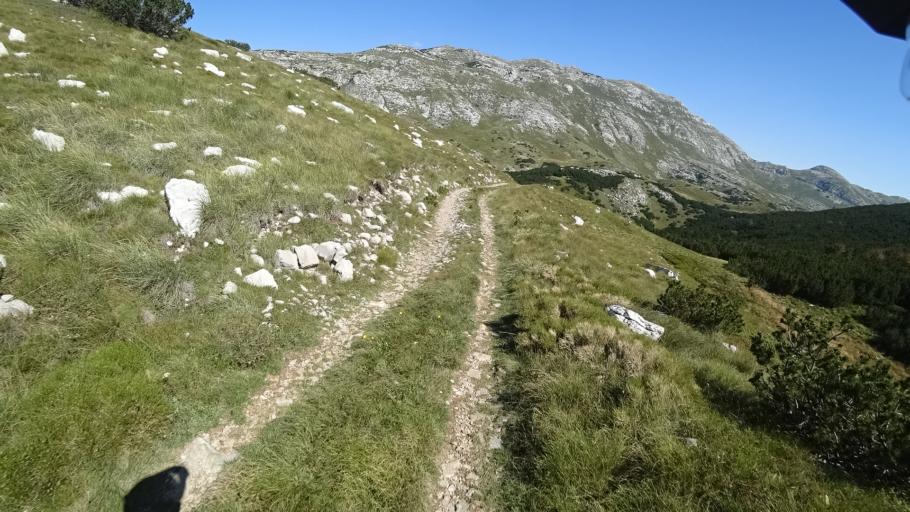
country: HR
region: Splitsko-Dalmatinska
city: Hrvace
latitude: 43.9376
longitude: 16.5754
